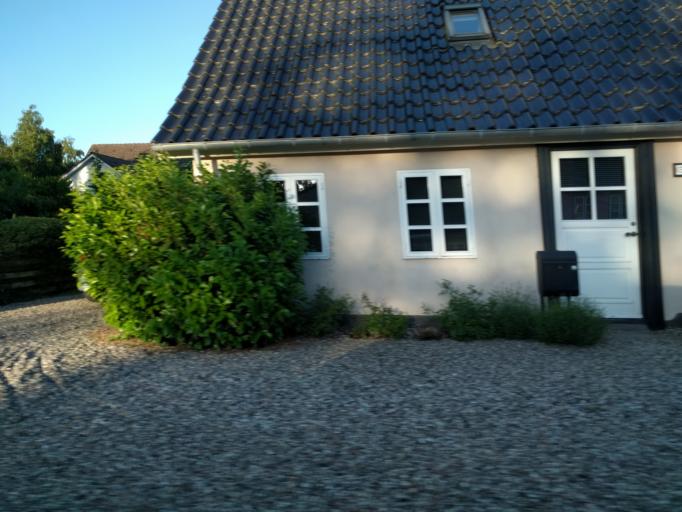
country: DK
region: South Denmark
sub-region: Kerteminde Kommune
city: Kerteminde
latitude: 55.5478
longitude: 10.6572
